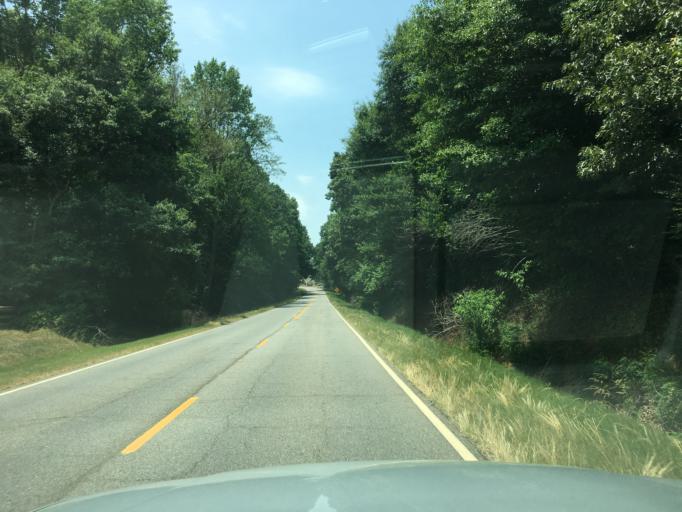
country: US
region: Georgia
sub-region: Madison County
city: Danielsville
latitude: 34.2207
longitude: -83.2224
